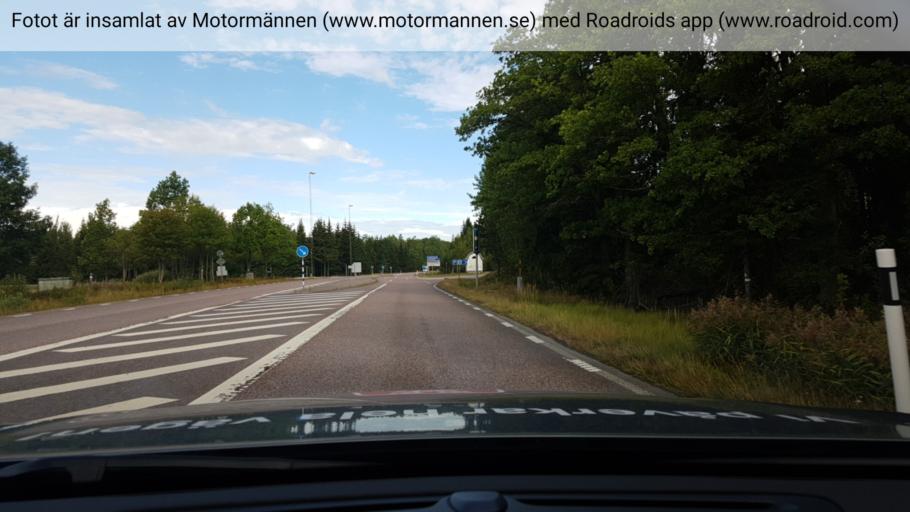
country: SE
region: Gaevleborg
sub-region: Gavle Kommun
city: Hedesunda
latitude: 60.2955
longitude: 16.9165
